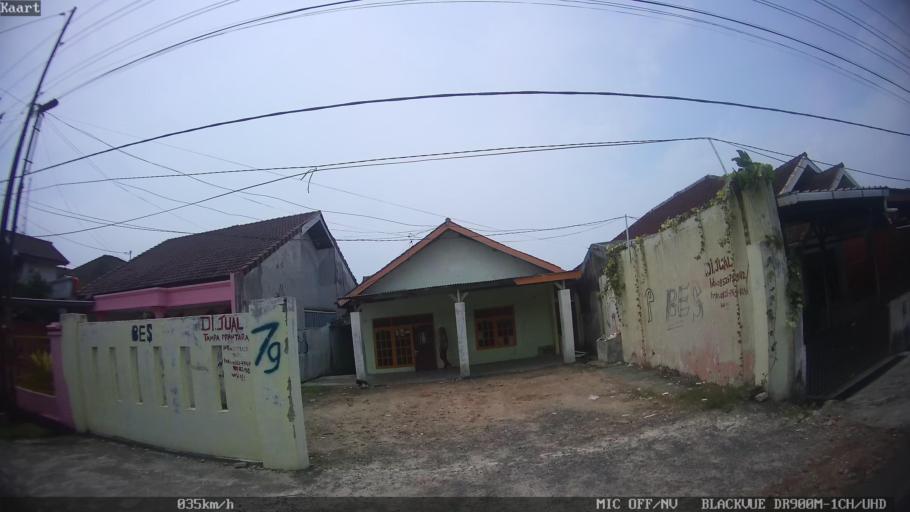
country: ID
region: Lampung
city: Bandarlampung
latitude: -5.4226
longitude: 105.2729
